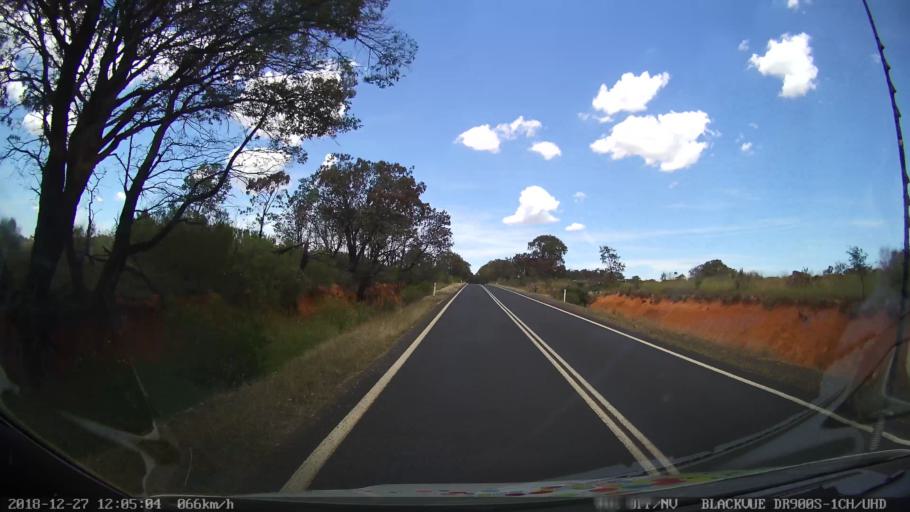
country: AU
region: New South Wales
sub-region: Blayney
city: Blayney
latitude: -33.8002
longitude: 149.3426
